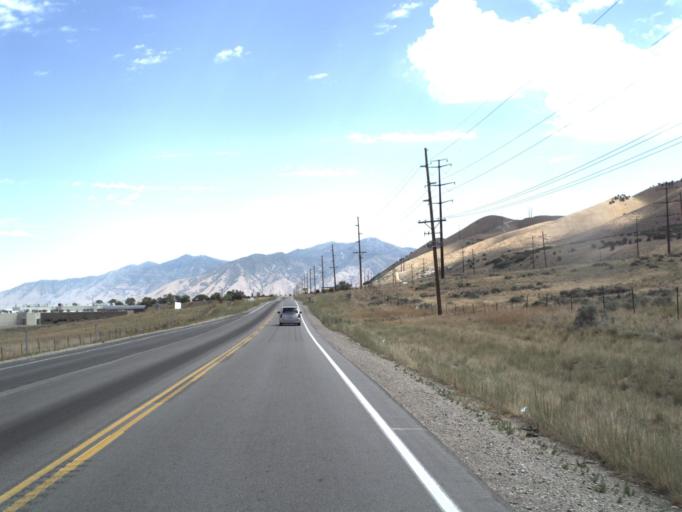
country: US
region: Utah
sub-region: Tooele County
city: Tooele
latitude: 40.4872
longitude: -112.3375
